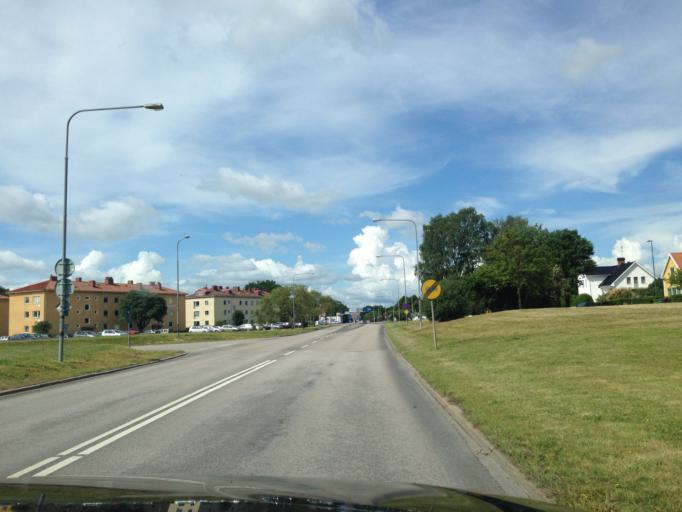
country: SE
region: Kalmar
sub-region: Kalmar Kommun
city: Kalmar
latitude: 56.6747
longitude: 16.3552
